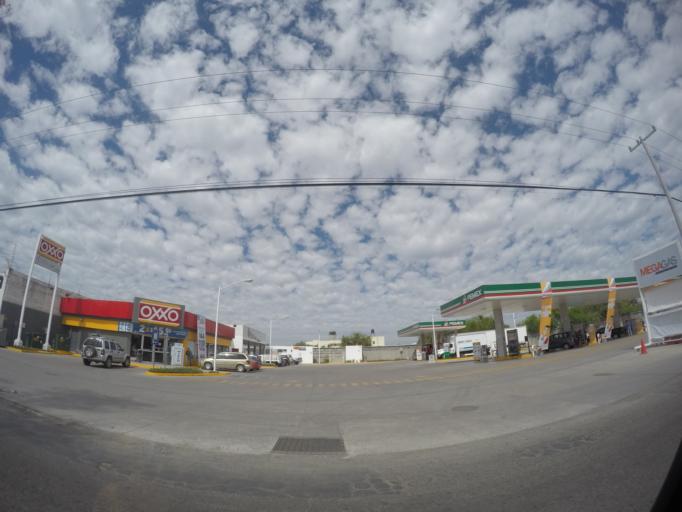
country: MX
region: Guanajuato
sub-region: Leon
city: San Jose de Duran (Los Troncoso)
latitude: 21.0859
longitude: -101.6798
